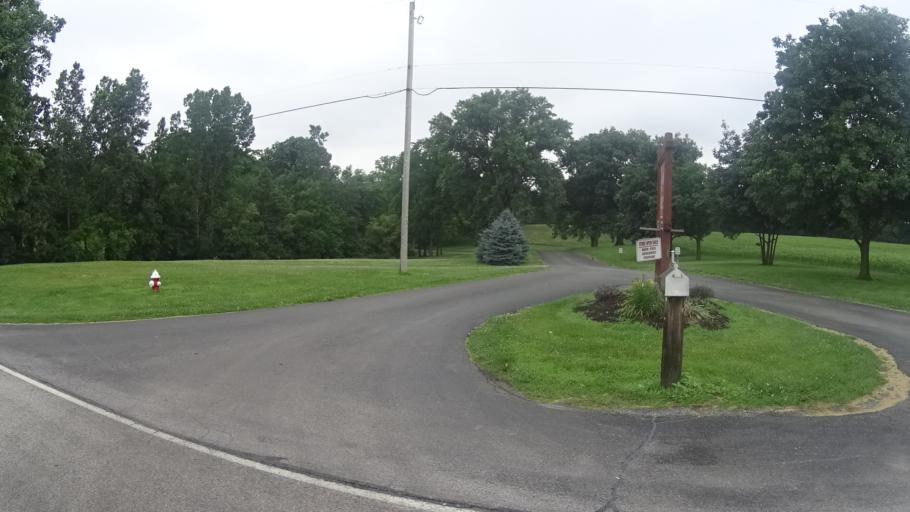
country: US
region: Ohio
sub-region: Erie County
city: Huron
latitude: 41.3566
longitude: -82.5492
